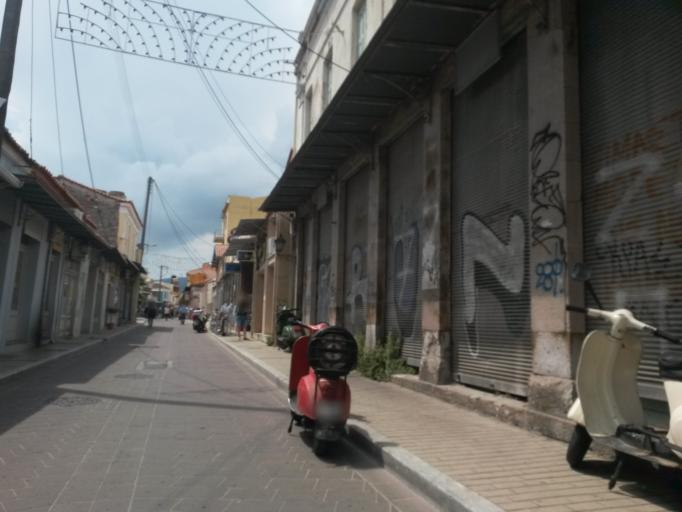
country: GR
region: North Aegean
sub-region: Nomos Lesvou
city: Mytilini
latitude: 39.1112
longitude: 26.5575
